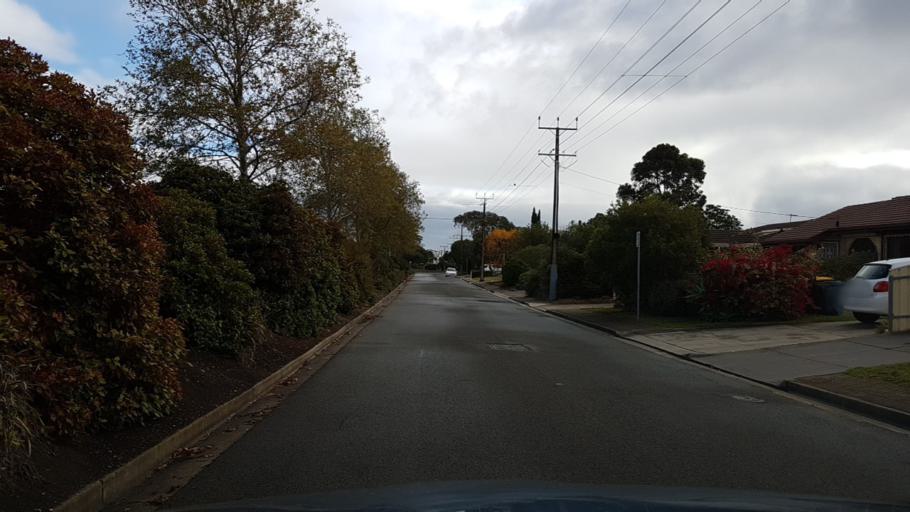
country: AU
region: South Australia
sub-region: Onkaparinga
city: Bedford Park
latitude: -35.0440
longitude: 138.5706
